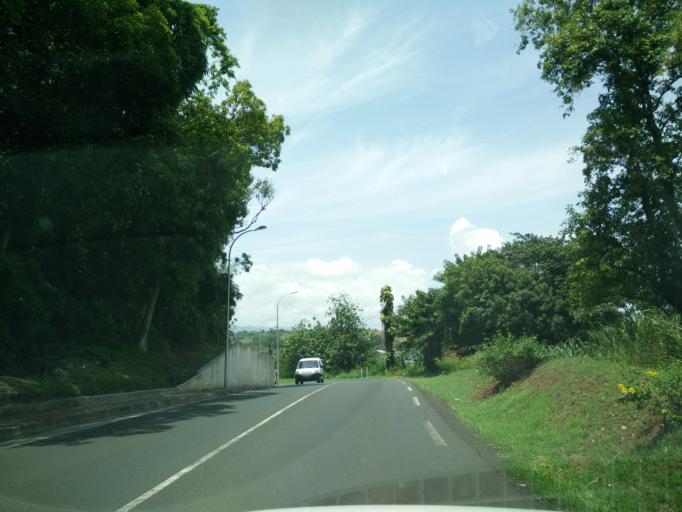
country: GP
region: Guadeloupe
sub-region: Guadeloupe
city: Petit-Bourg
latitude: 16.1980
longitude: -61.6019
